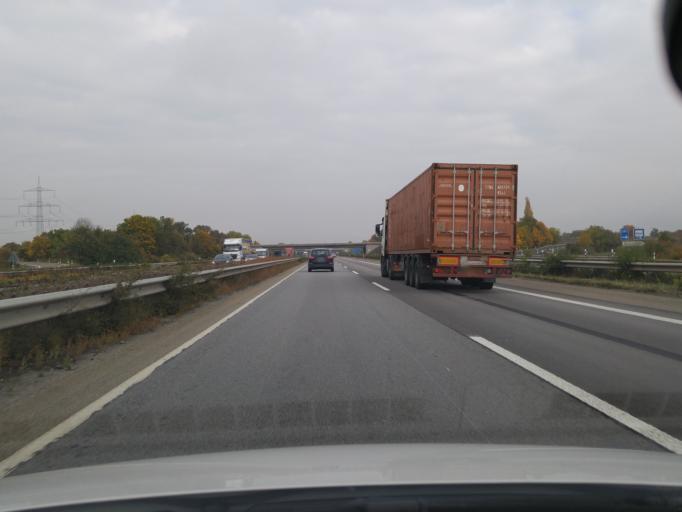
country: DE
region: Rheinland-Pfalz
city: Fussgonheim
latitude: 49.4735
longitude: 8.3128
